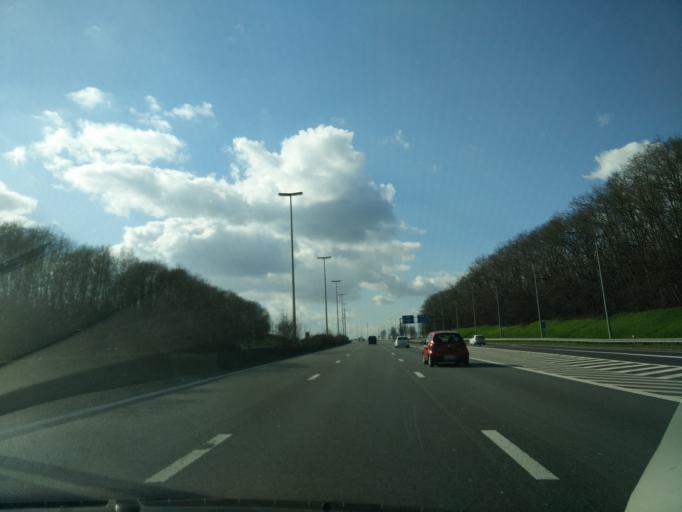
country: BE
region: Flanders
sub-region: Provincie Vlaams-Brabant
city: Bertem
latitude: 50.8552
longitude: 4.6508
